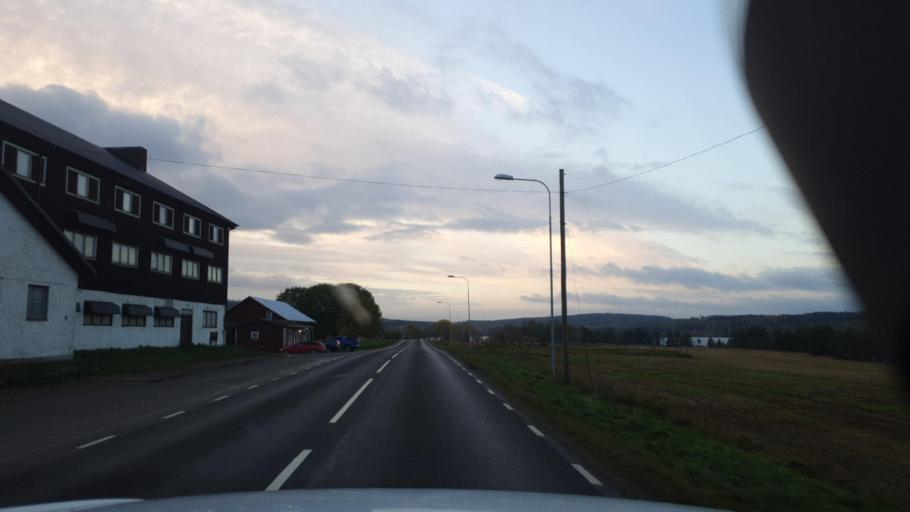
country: SE
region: Vaermland
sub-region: Arvika Kommun
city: Arvika
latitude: 59.7578
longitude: 12.5453
